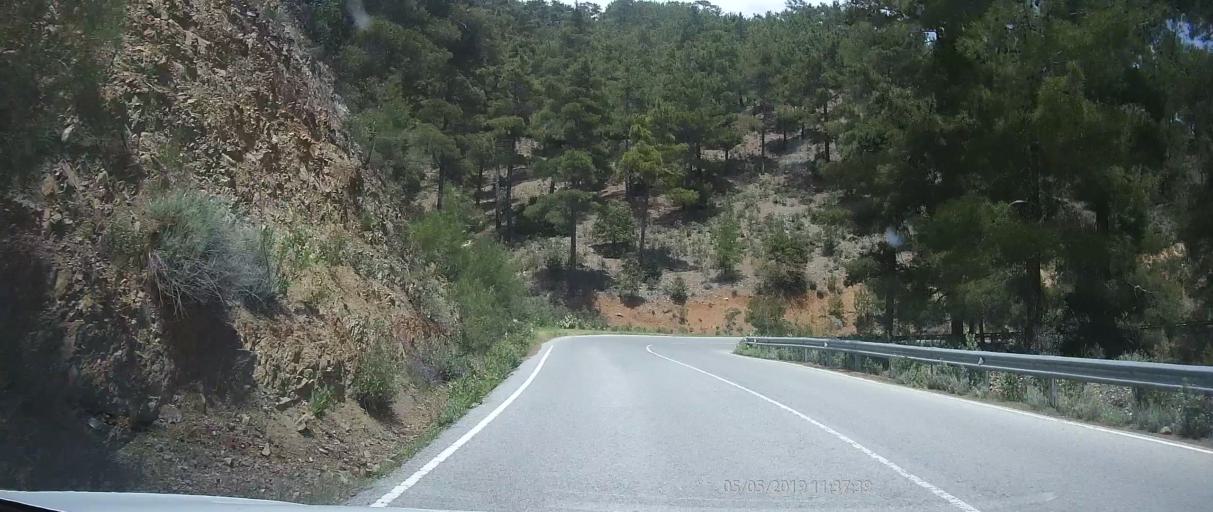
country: CY
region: Lefkosia
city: Kato Pyrgos
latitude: 34.9747
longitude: 32.6588
